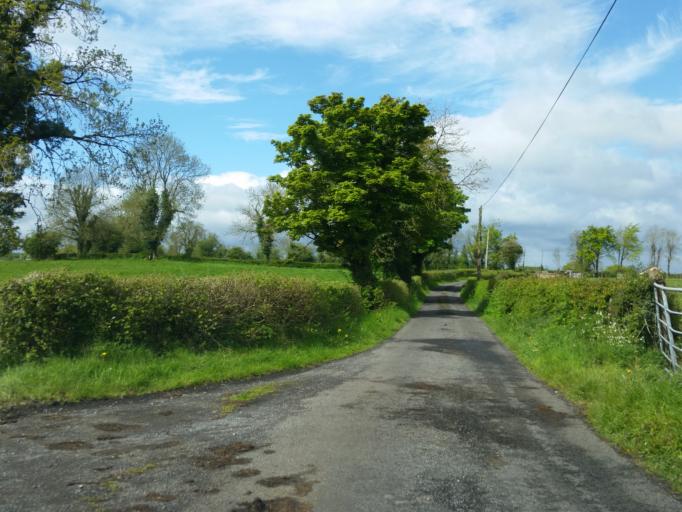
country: GB
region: Northern Ireland
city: Lisnaskea
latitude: 54.2562
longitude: -7.4046
